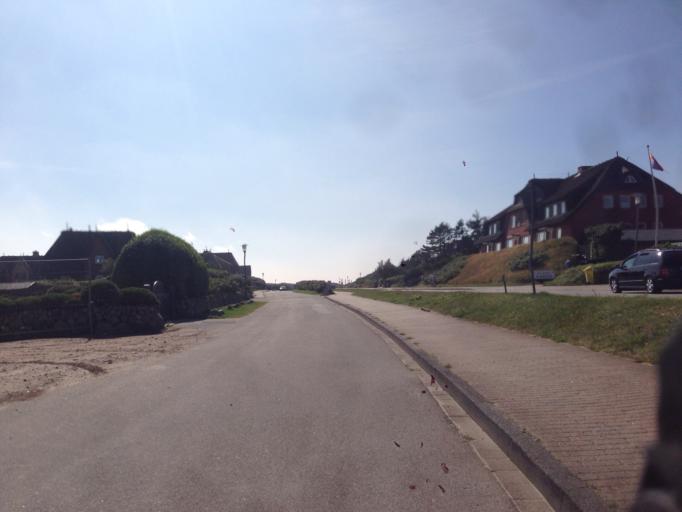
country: DE
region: Schleswig-Holstein
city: Westerland
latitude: 54.8434
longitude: 8.2928
